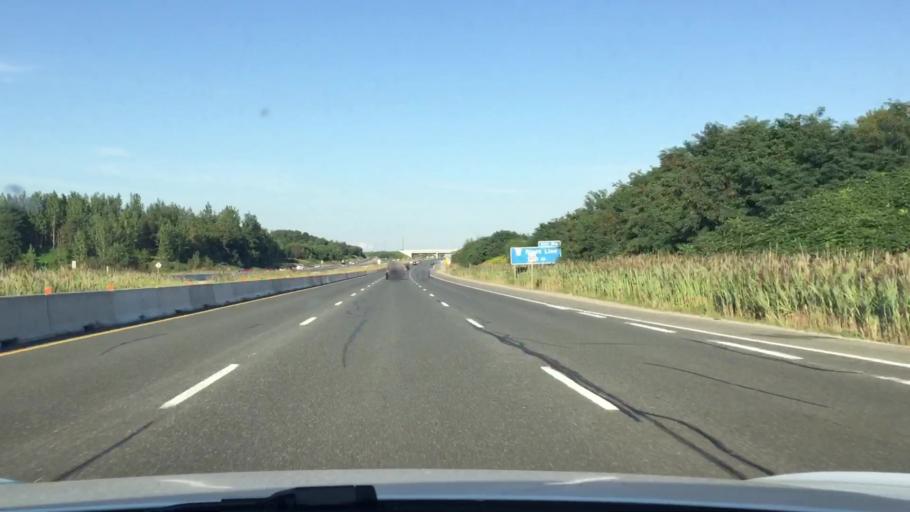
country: CA
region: Ontario
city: Markham
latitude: 43.8668
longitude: -79.2471
